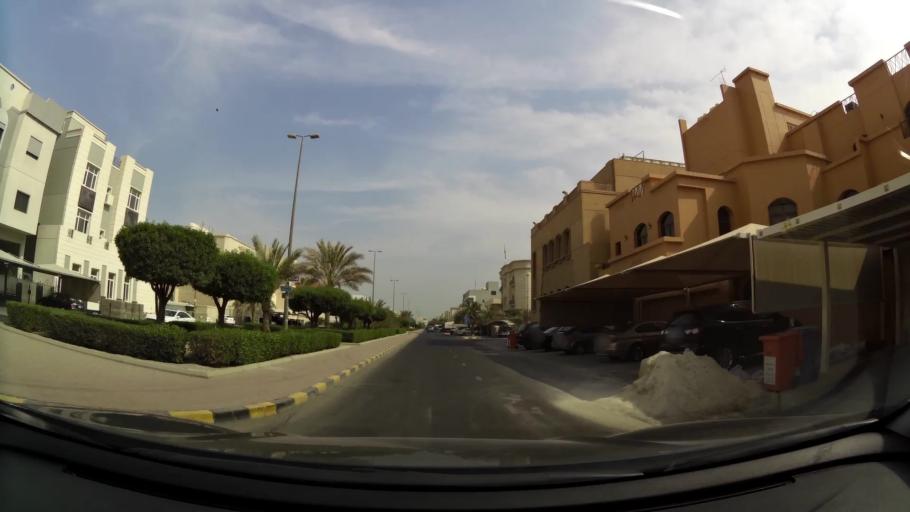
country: KW
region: Al Asimah
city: Ash Shamiyah
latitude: 29.3364
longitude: 47.9645
